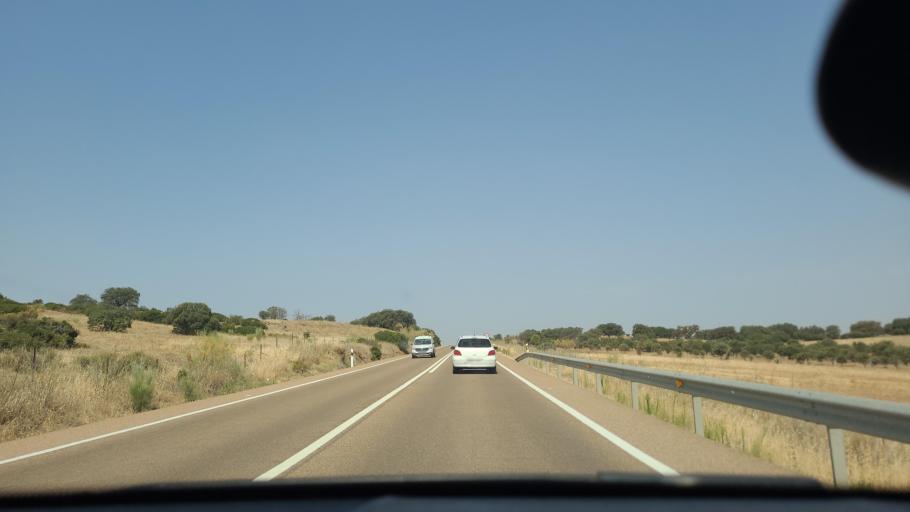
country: ES
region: Extremadura
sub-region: Provincia de Badajoz
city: Usagre
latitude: 38.3637
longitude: -6.2282
